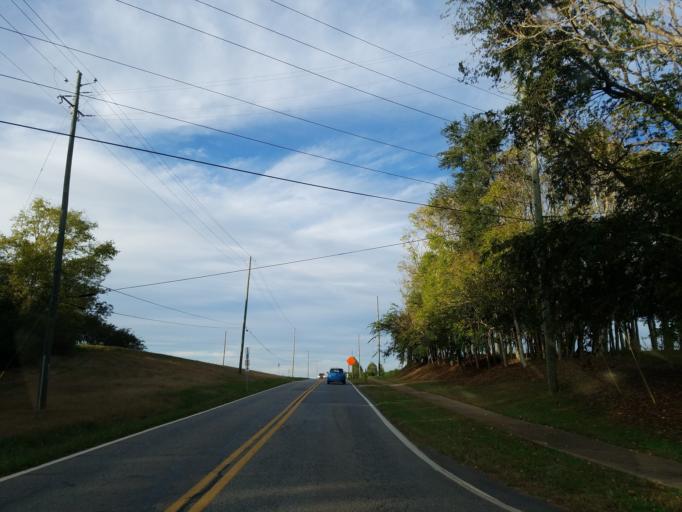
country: US
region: Georgia
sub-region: Bartow County
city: Cartersville
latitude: 34.1264
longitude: -84.8205
